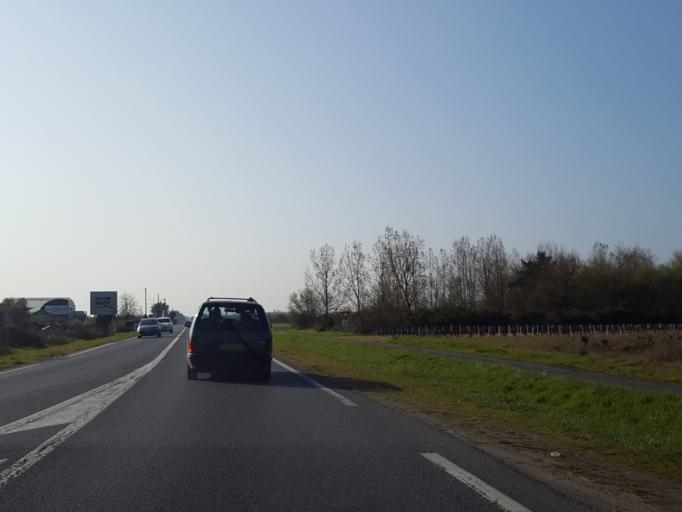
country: FR
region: Pays de la Loire
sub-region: Departement de la Loire-Atlantique
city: Les Sorinieres
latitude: 47.1103
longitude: -1.5388
